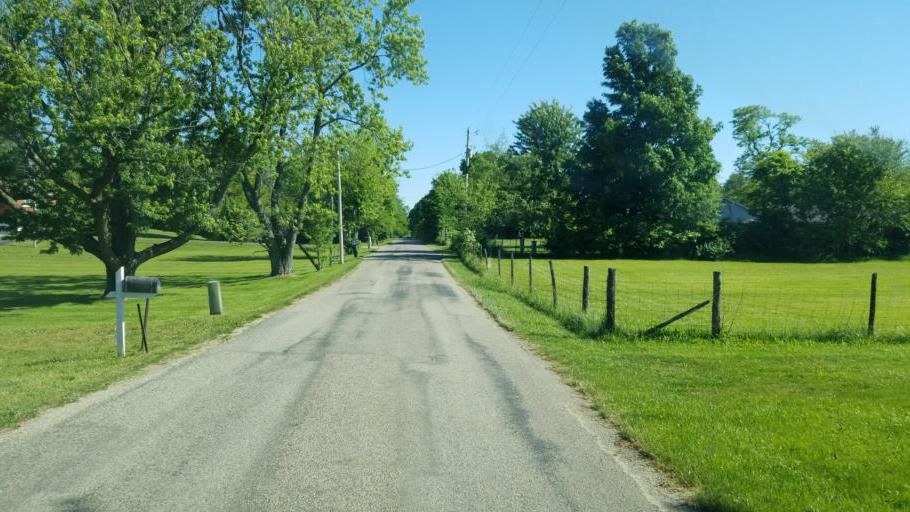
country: US
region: Ohio
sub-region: Preble County
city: New Paris
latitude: 39.8687
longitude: -84.8324
